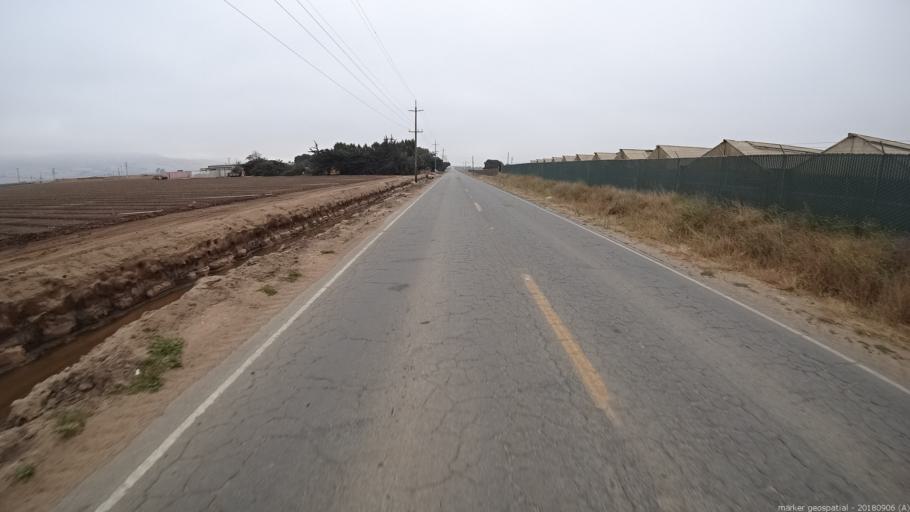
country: US
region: California
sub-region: Monterey County
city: Chualar
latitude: 36.6385
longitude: -121.5646
